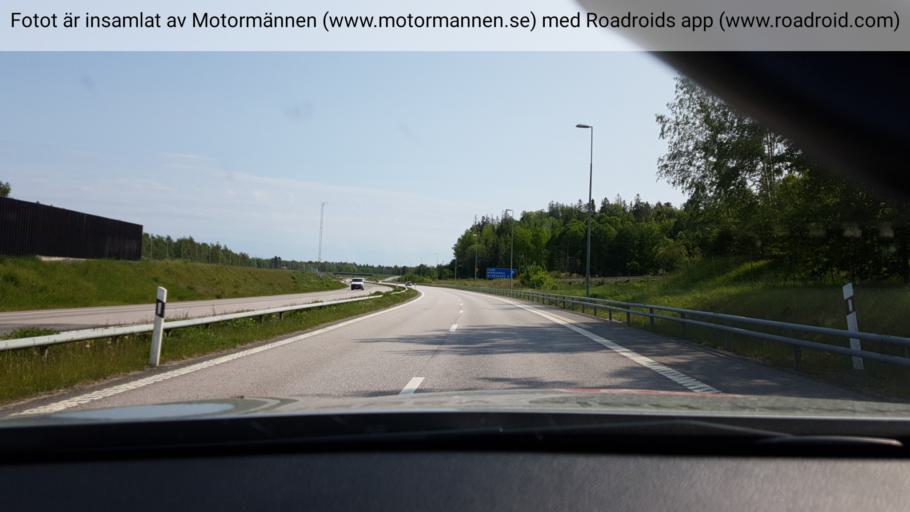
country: SE
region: Stockholm
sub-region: Nynashamns Kommun
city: Osmo
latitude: 58.9491
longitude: 17.9024
